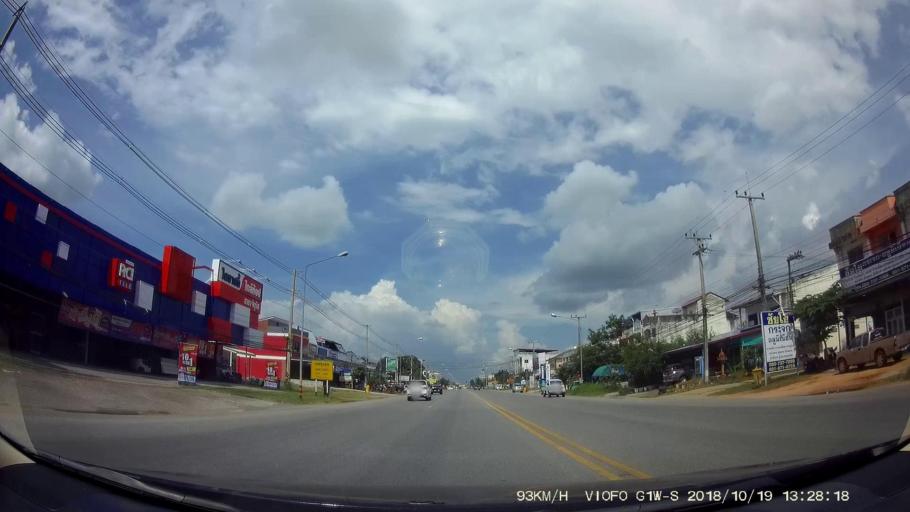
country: TH
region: Chaiyaphum
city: Chatturat
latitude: 15.5604
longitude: 101.8477
